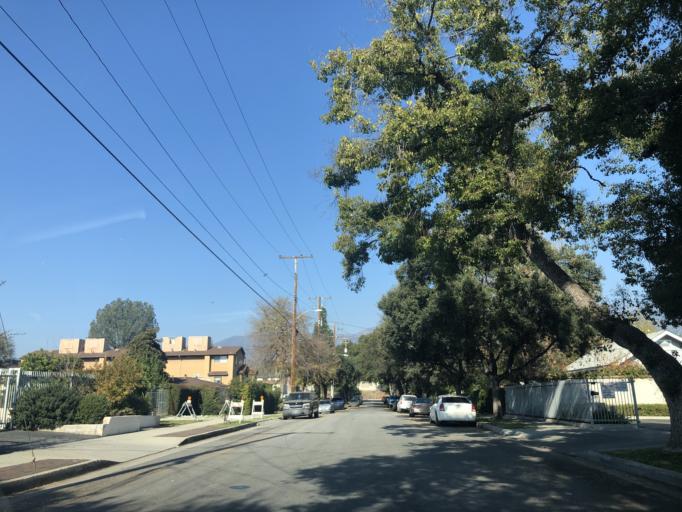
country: US
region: California
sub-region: Los Angeles County
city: Pasadena
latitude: 34.1498
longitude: -118.1244
